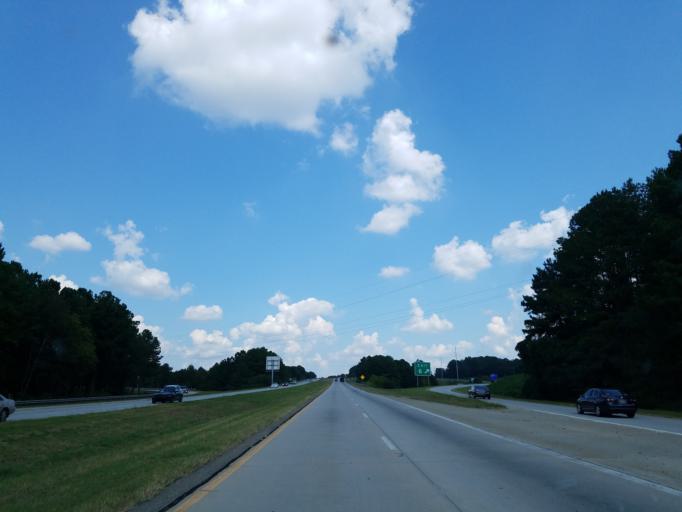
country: US
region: Georgia
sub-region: Clarke County
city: Athens
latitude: 33.9189
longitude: -83.3824
